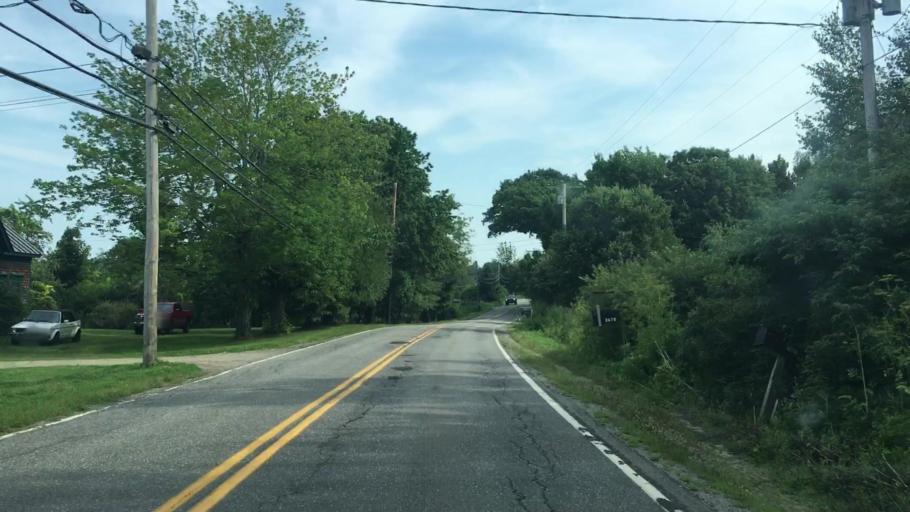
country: US
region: Maine
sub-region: Knox County
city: Friendship
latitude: 44.0383
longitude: -69.3294
